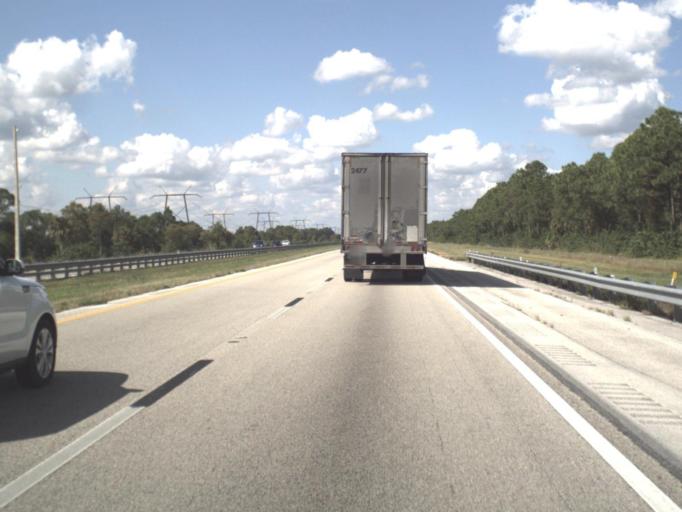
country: US
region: Florida
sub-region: Indian River County
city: West Vero Corridor
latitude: 27.5420
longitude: -80.6214
